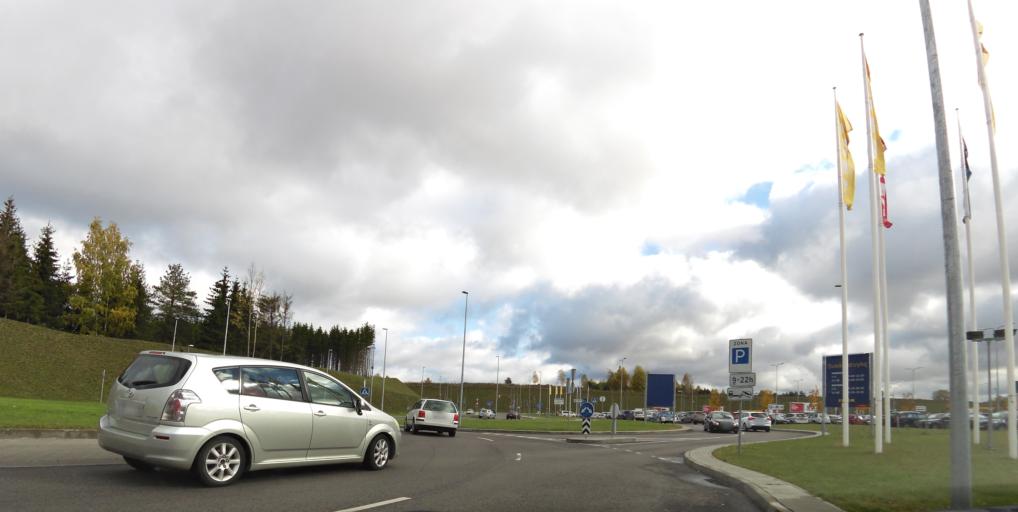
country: LT
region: Vilnius County
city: Naujamiestis
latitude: 54.6531
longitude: 25.2791
